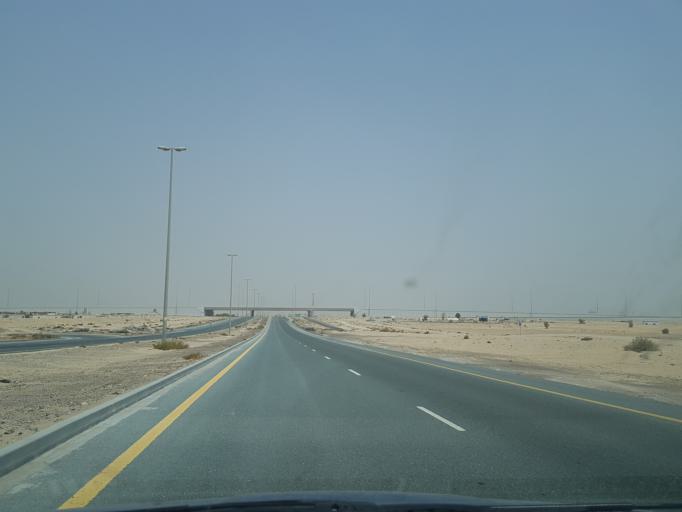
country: AE
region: Dubai
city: Dubai
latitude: 25.0542
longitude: 55.3047
